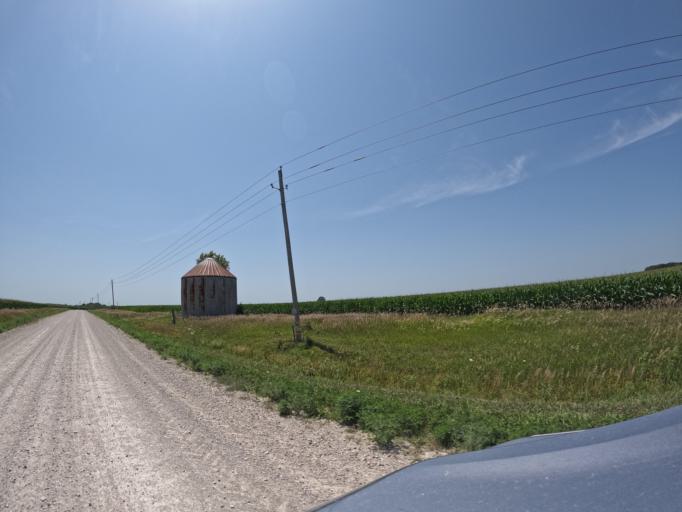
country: US
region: Iowa
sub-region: Henry County
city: Mount Pleasant
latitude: 40.9119
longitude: -91.6465
